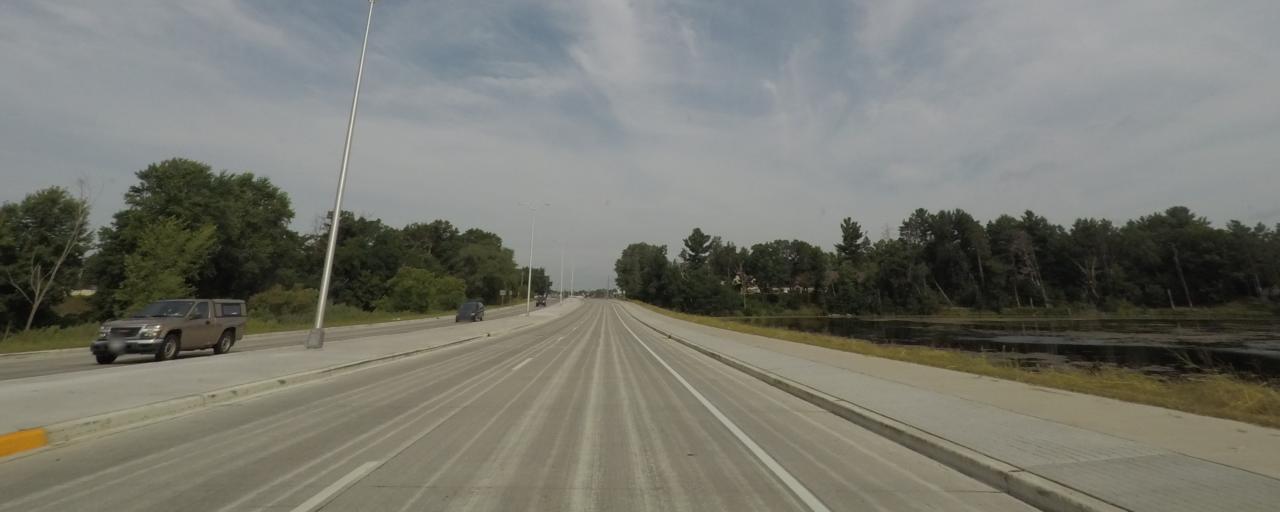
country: US
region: Wisconsin
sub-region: Portage County
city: Whiting
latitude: 44.4950
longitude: -89.5557
